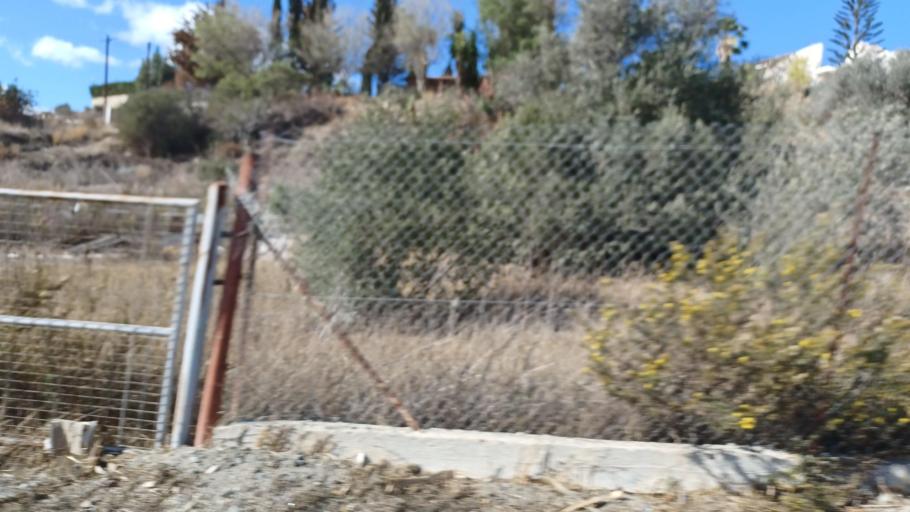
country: CY
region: Limassol
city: Pyrgos
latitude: 34.7437
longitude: 33.2113
